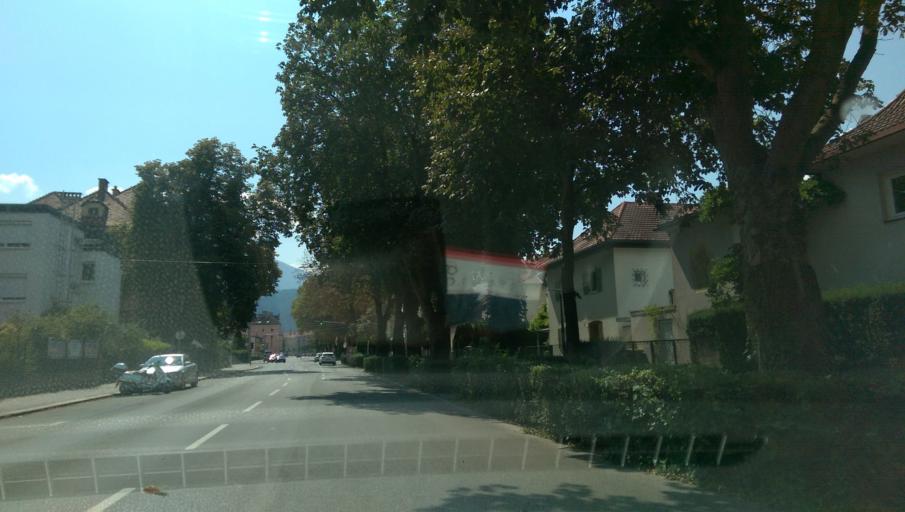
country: AT
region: Tyrol
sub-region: Innsbruck Stadt
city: Innsbruck
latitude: 47.2712
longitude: 11.4108
